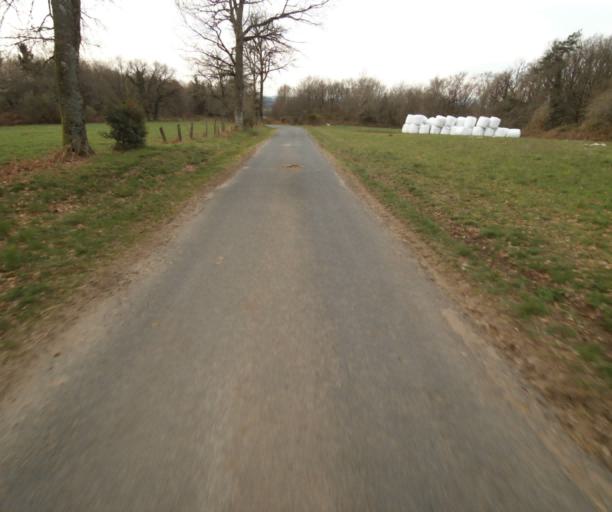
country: FR
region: Limousin
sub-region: Departement de la Correze
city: Correze
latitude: 45.4424
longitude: 1.8213
